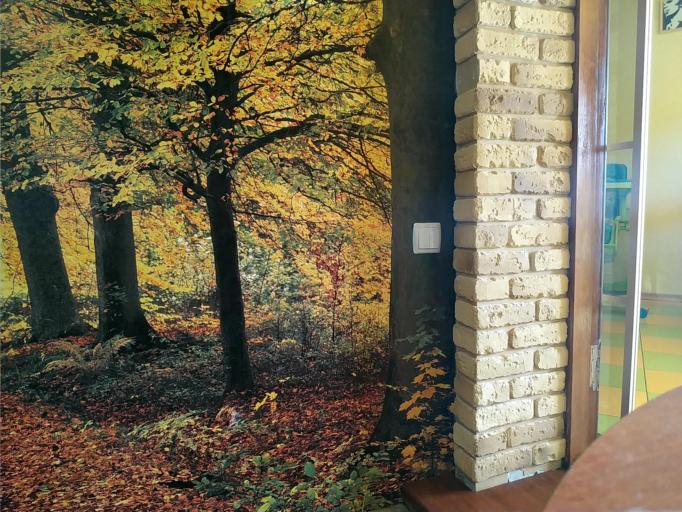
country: RU
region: Smolensk
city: Katyn'
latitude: 54.9949
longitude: 31.7498
